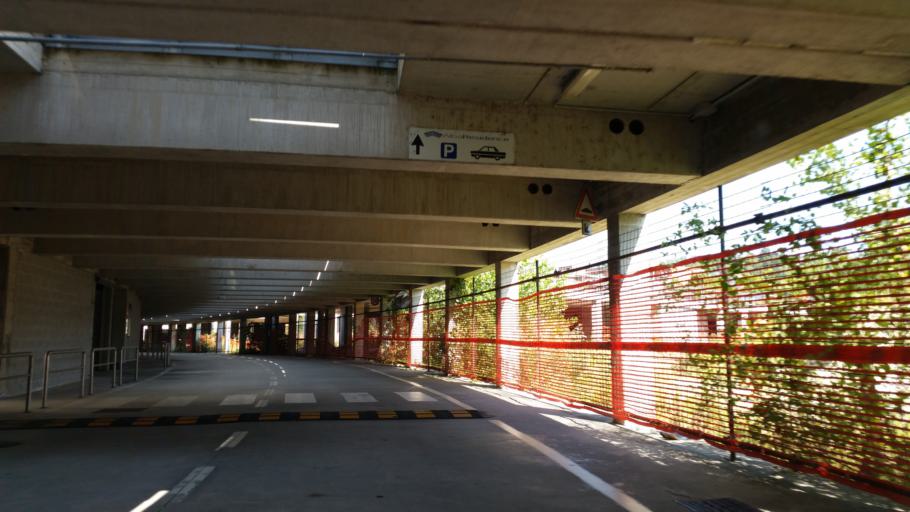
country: IT
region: Piedmont
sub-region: Provincia di Cuneo
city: Alba
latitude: 44.6913
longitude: 8.0162
